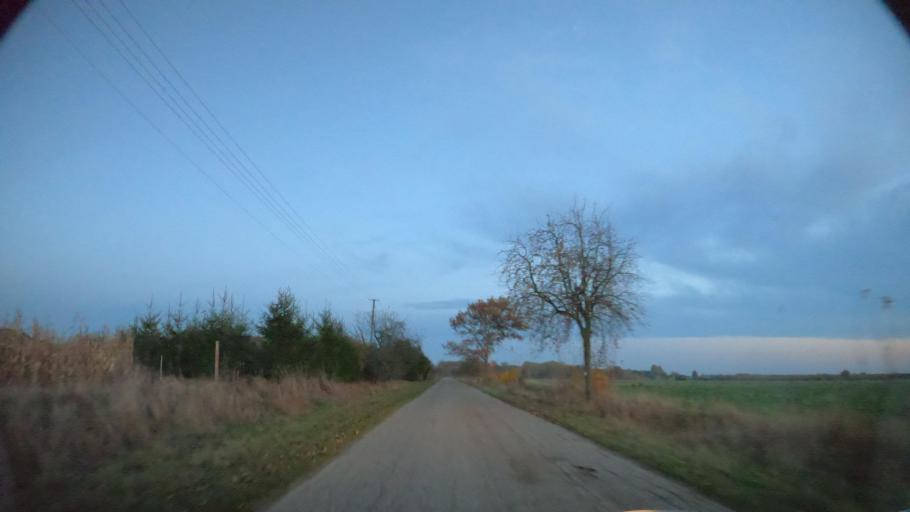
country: PL
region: Greater Poland Voivodeship
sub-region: Powiat zlotowski
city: Sypniewo
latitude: 53.4257
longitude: 16.6321
